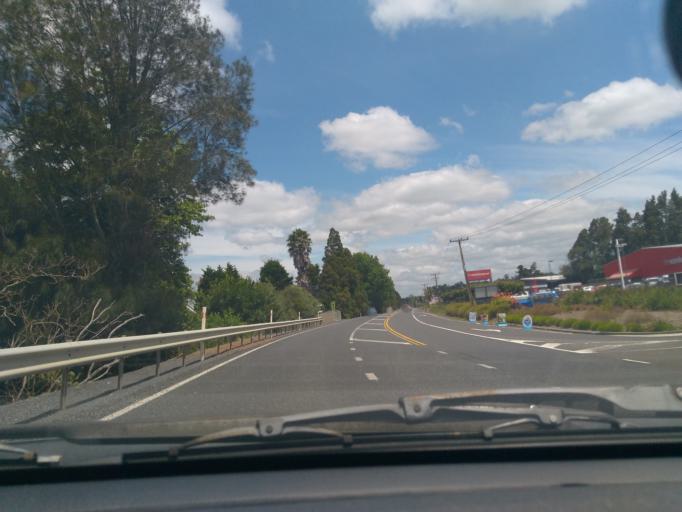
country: NZ
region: Northland
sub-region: Far North District
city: Kerikeri
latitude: -35.2094
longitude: 173.9202
